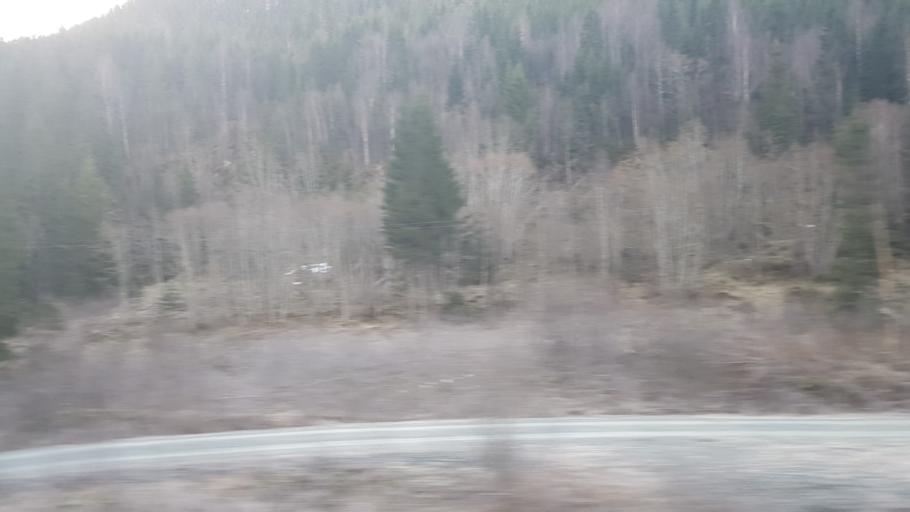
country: NO
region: Nord-Trondelag
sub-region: Stjordal
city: Stjordalshalsen
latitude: 63.5896
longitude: 11.0119
